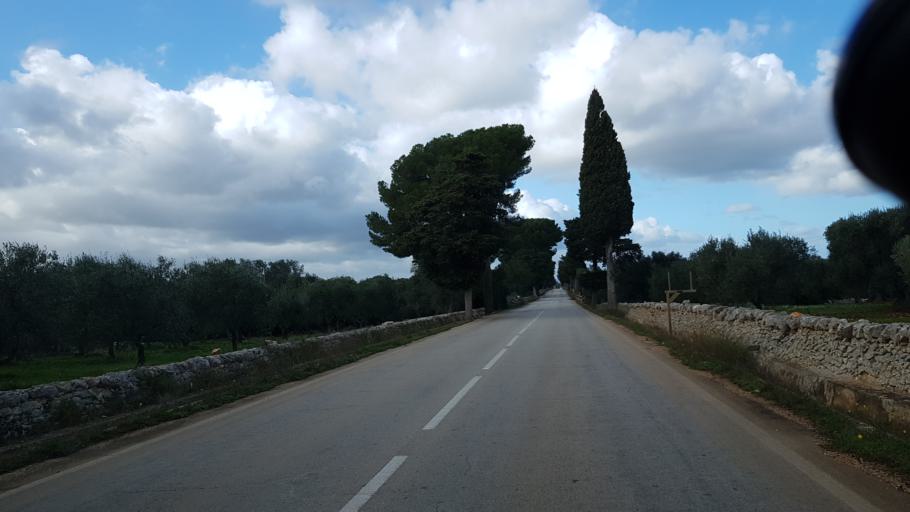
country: IT
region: Apulia
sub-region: Provincia di Brindisi
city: Montalbano
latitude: 40.7685
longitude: 17.5111
